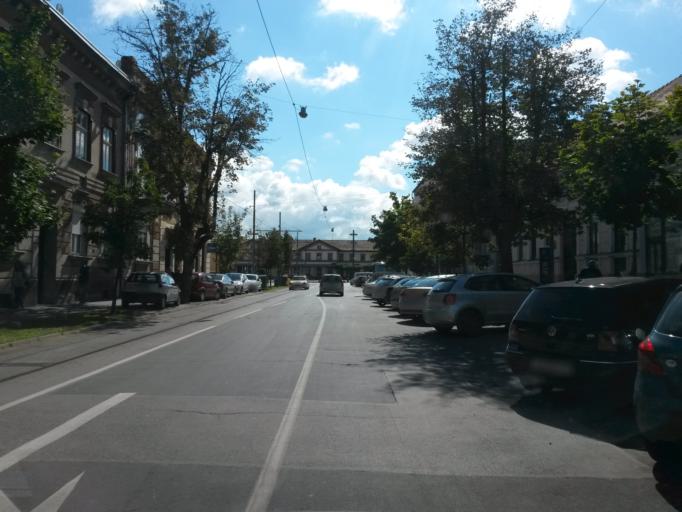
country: HR
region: Osjecko-Baranjska
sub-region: Grad Osijek
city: Osijek
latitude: 45.5544
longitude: 18.6831
